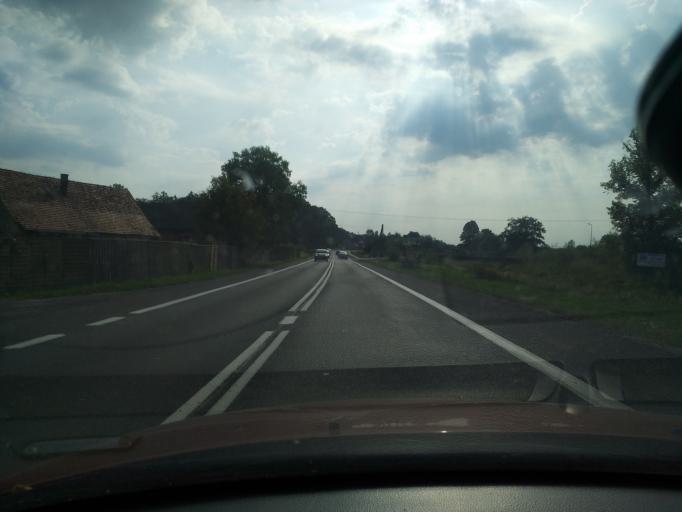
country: PL
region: Lower Silesian Voivodeship
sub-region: Powiat lubanski
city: Olszyna
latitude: 51.0830
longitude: 15.3285
